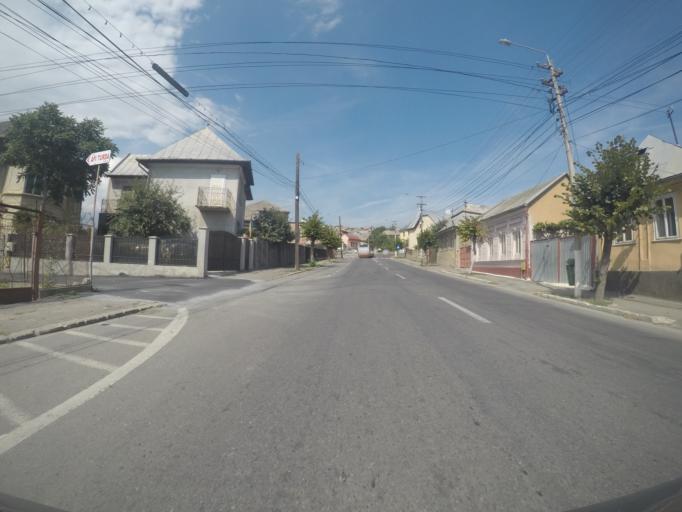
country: RO
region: Cluj
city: Turda
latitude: 46.5749
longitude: 23.7876
